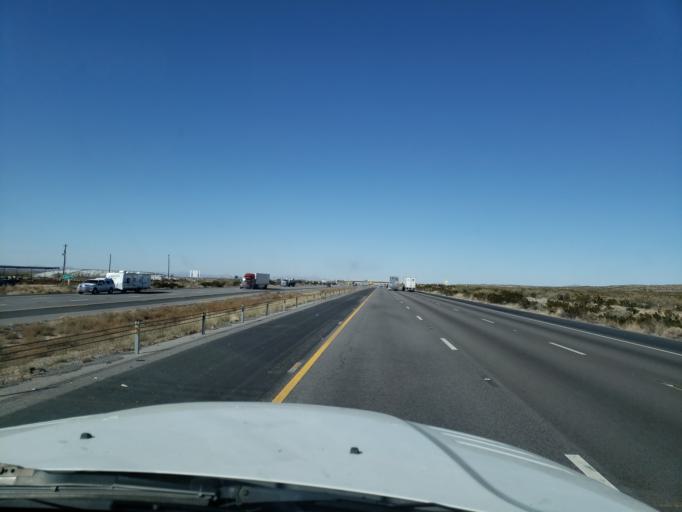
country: US
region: New Mexico
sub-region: Dona Ana County
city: Mesquite
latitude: 32.1676
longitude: -106.6651
